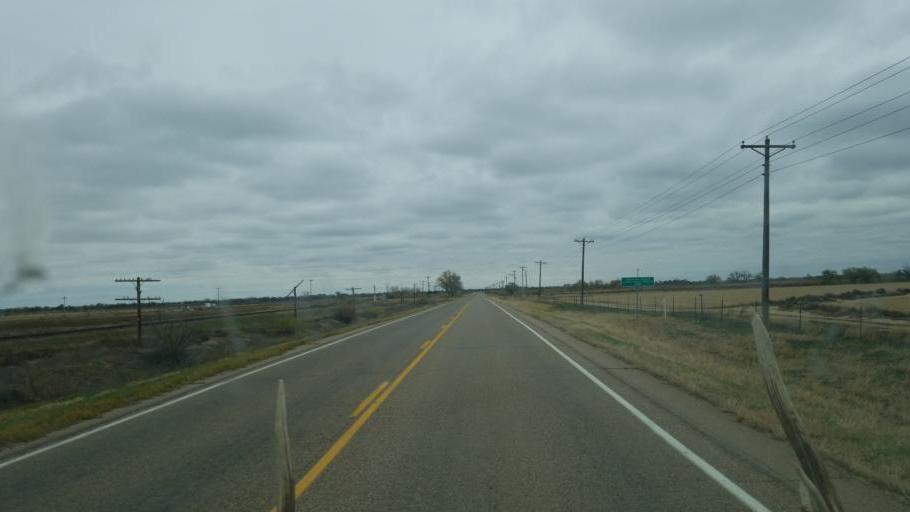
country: US
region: Colorado
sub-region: Crowley County
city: Ordway
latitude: 38.1962
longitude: -103.8420
